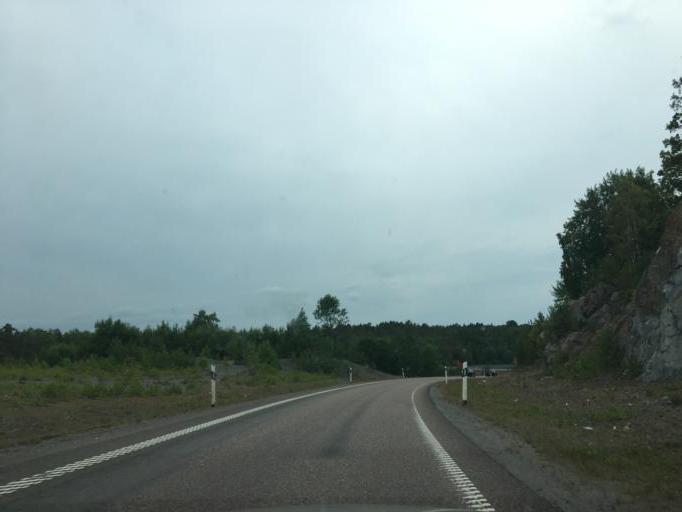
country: SE
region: Soedermanland
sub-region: Strangnas Kommun
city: Strangnas
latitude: 59.3687
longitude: 16.9562
